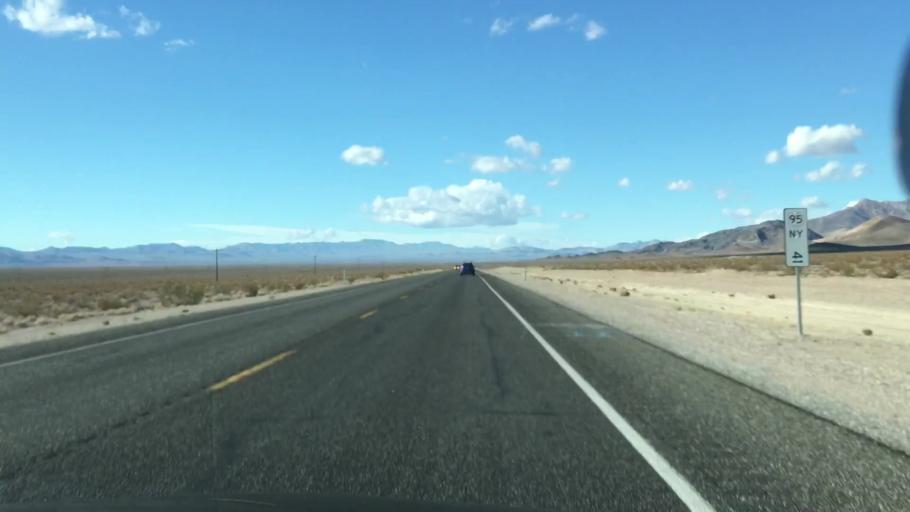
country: US
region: Nevada
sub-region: Nye County
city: Beatty
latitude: 36.6984
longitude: -116.5784
